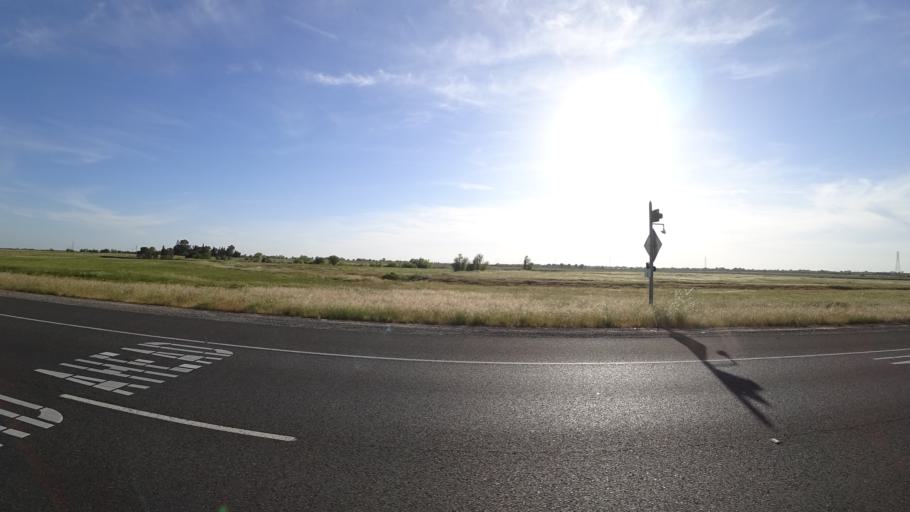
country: US
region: California
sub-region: Placer County
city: Sheridan
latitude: 38.9815
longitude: -121.3838
